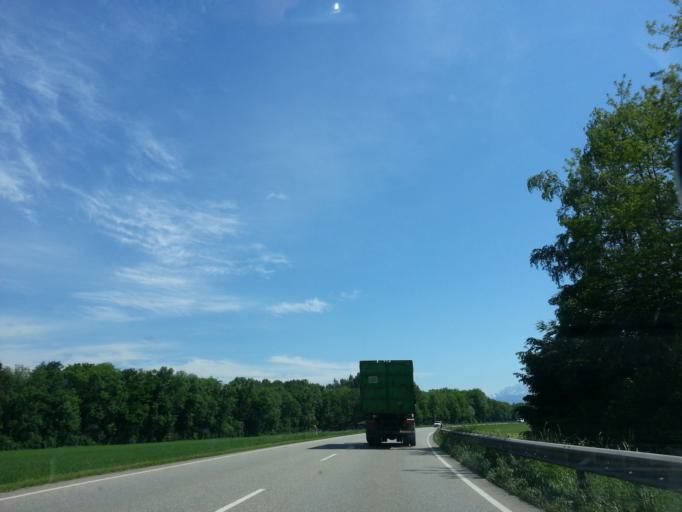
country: DE
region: Bavaria
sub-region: Upper Bavaria
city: Freilassing
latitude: 47.8510
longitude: 12.9937
